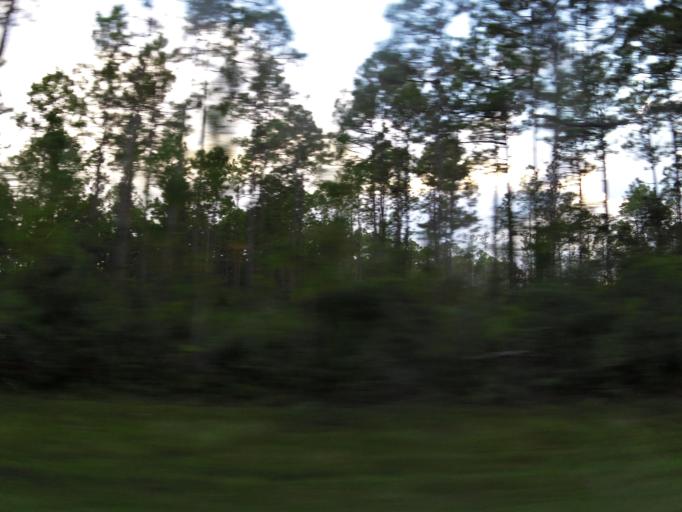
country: US
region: Georgia
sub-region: Echols County
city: Statenville
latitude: 30.7415
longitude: -83.0985
